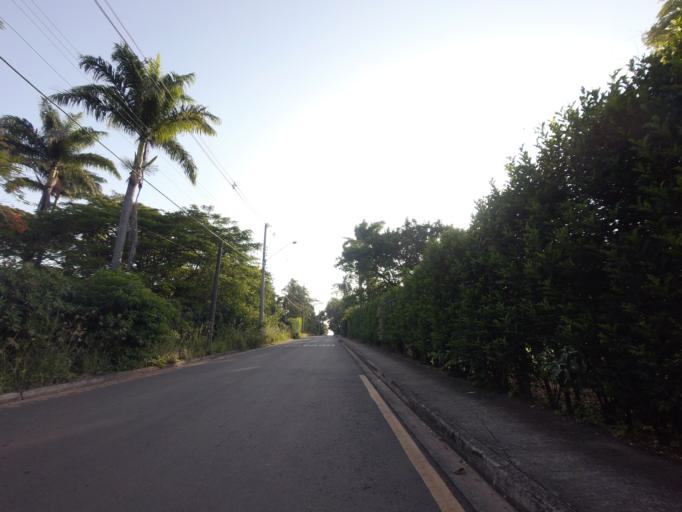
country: BR
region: Sao Paulo
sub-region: Piracicaba
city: Piracicaba
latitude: -22.7448
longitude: -47.6062
